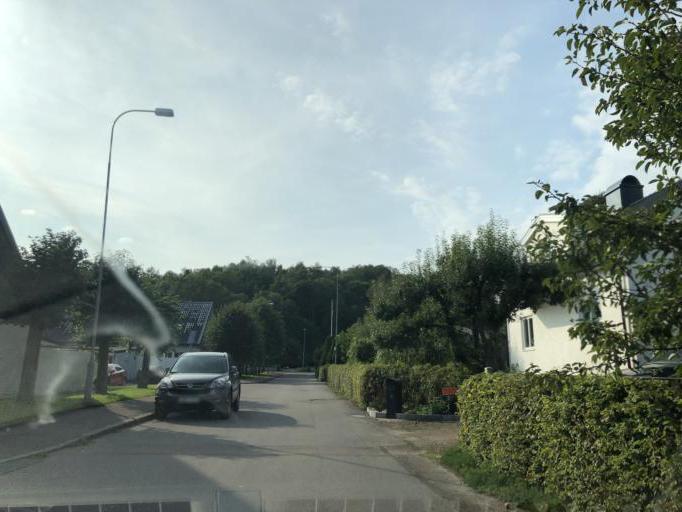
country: SE
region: Vaestra Goetaland
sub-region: Goteborg
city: Goeteborg
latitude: 57.7377
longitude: 11.9829
